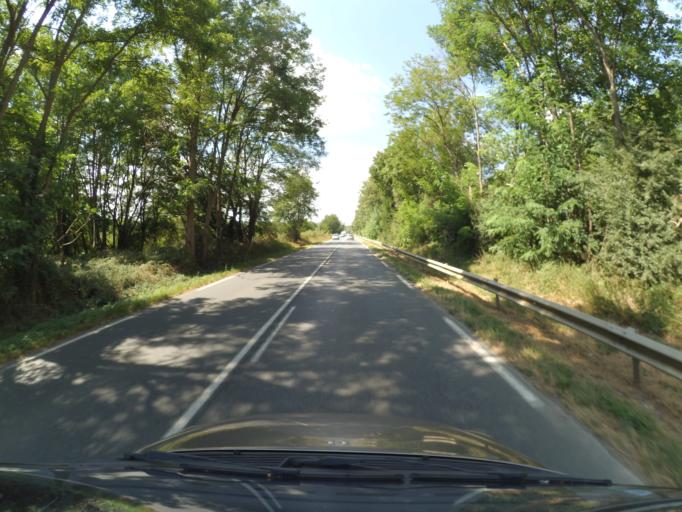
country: FR
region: Poitou-Charentes
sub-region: Departement de la Vienne
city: Lussac-les-Chateaux
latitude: 46.4130
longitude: 0.6864
